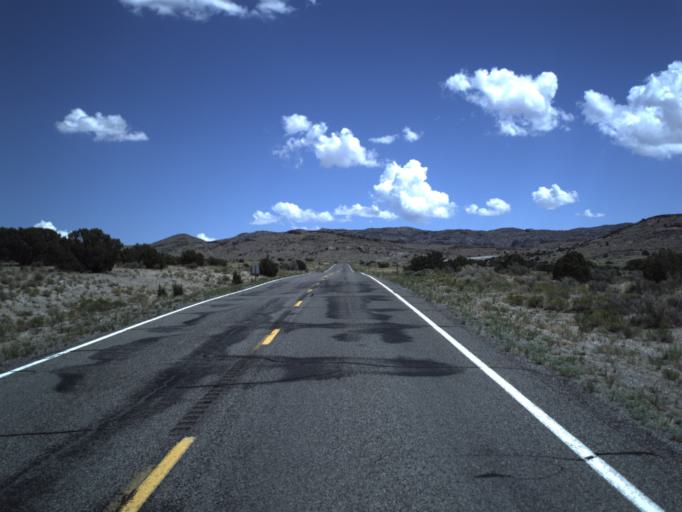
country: US
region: Utah
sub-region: Beaver County
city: Milford
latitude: 39.0763
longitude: -113.7111
